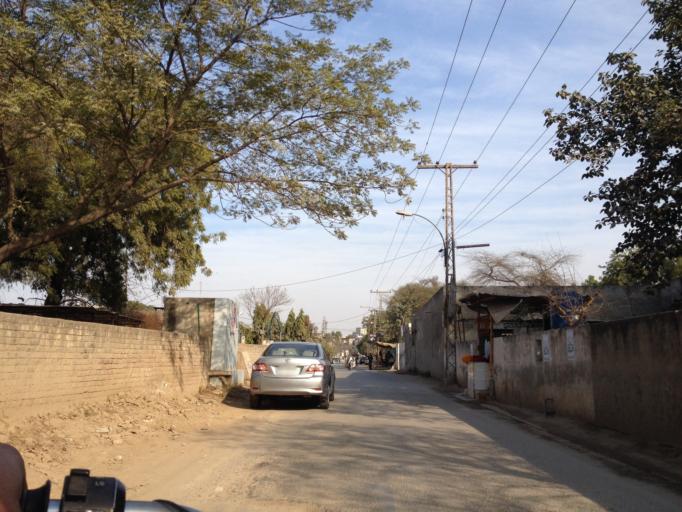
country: PK
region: Punjab
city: Lahore
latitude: 31.5035
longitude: 74.3158
